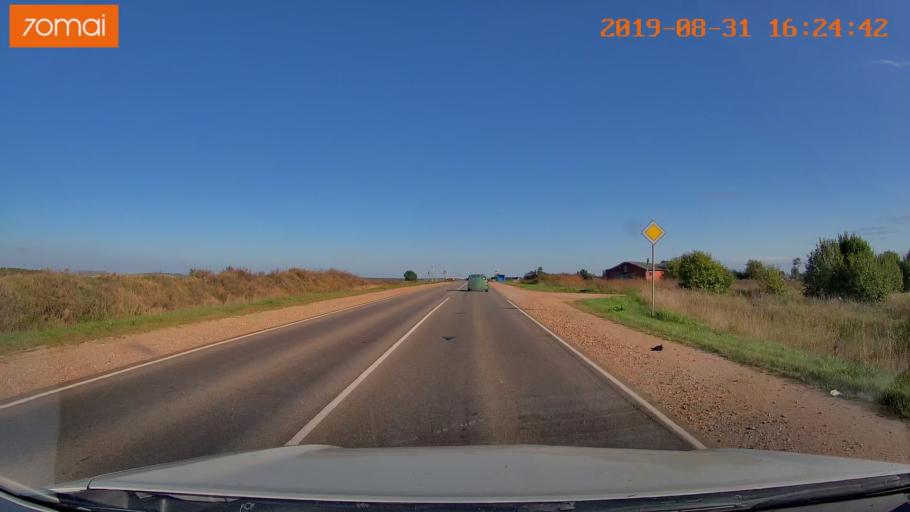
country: RU
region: Kaluga
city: Babynino
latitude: 54.5212
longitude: 35.6994
